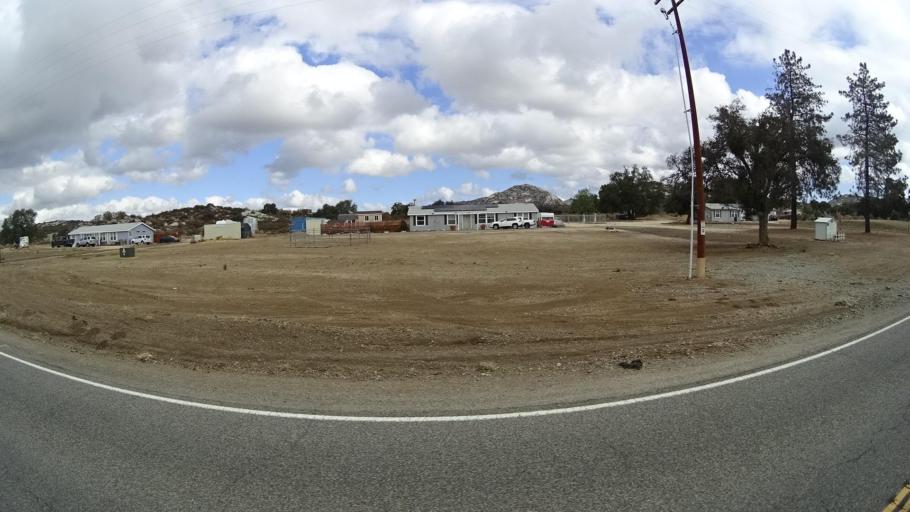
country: US
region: California
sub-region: San Diego County
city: Campo
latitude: 32.6302
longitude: -116.4533
